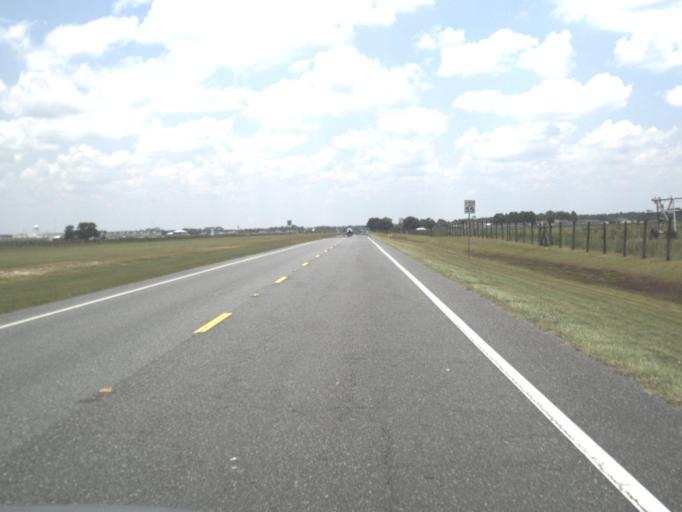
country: US
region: Florida
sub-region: Bradford County
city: Starke
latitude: 30.0495
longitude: -82.1722
